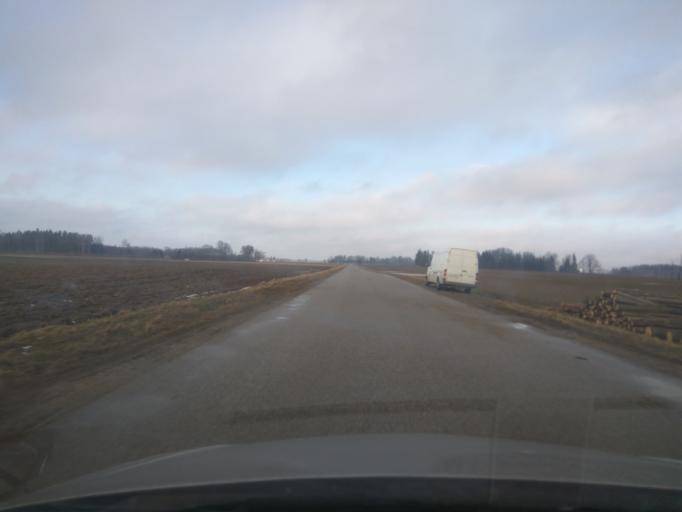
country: LV
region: Saldus Rajons
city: Saldus
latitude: 56.7869
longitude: 22.3876
